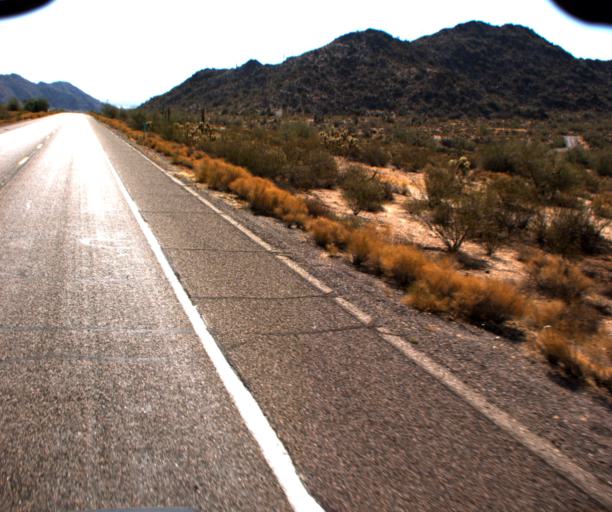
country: US
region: Arizona
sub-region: Pinal County
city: Sacaton
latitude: 33.0131
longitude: -111.6824
